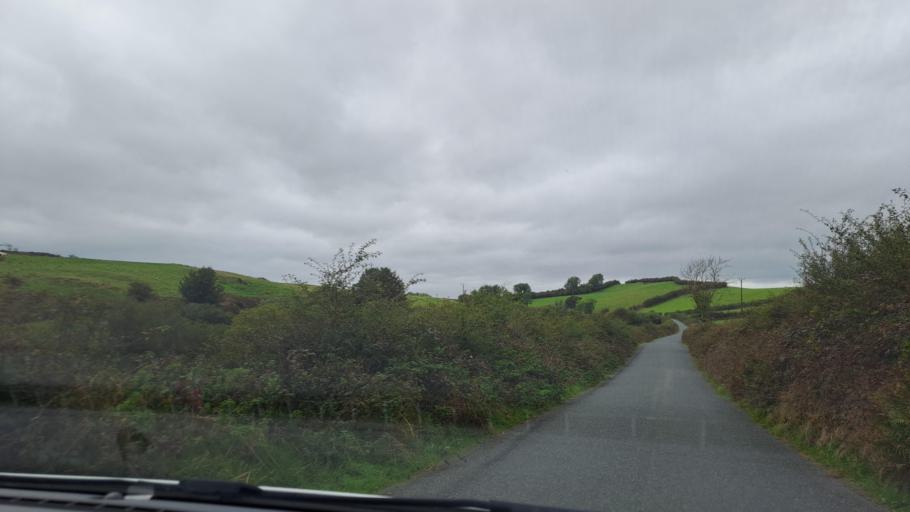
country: IE
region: Ulster
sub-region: An Cabhan
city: Kingscourt
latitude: 54.0186
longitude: -6.8629
